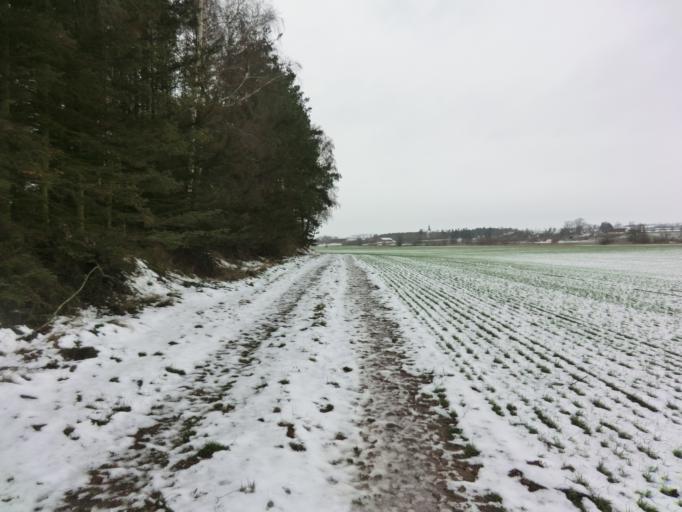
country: SE
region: Skane
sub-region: Hoors Kommun
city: Loberod
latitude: 55.7381
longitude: 13.4056
